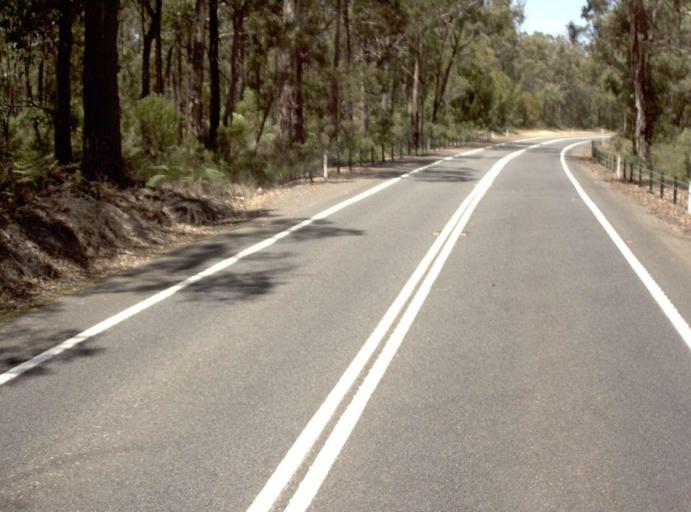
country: AU
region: Victoria
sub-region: East Gippsland
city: Lakes Entrance
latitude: -37.8245
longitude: 148.0325
